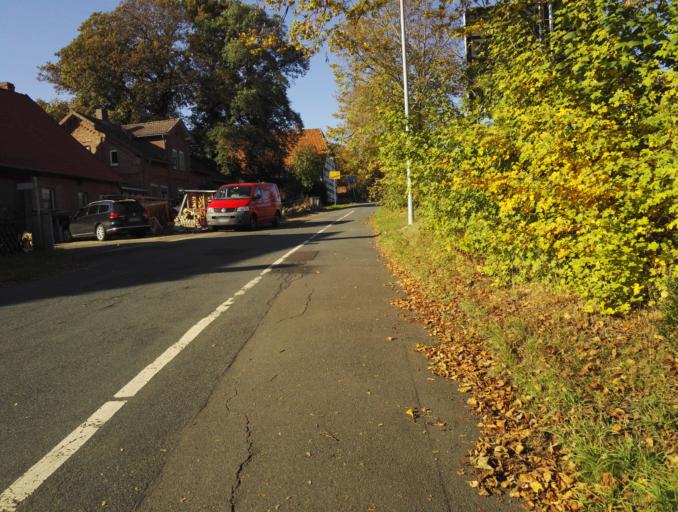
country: DE
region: Lower Saxony
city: Holle
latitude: 52.1080
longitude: 10.1091
